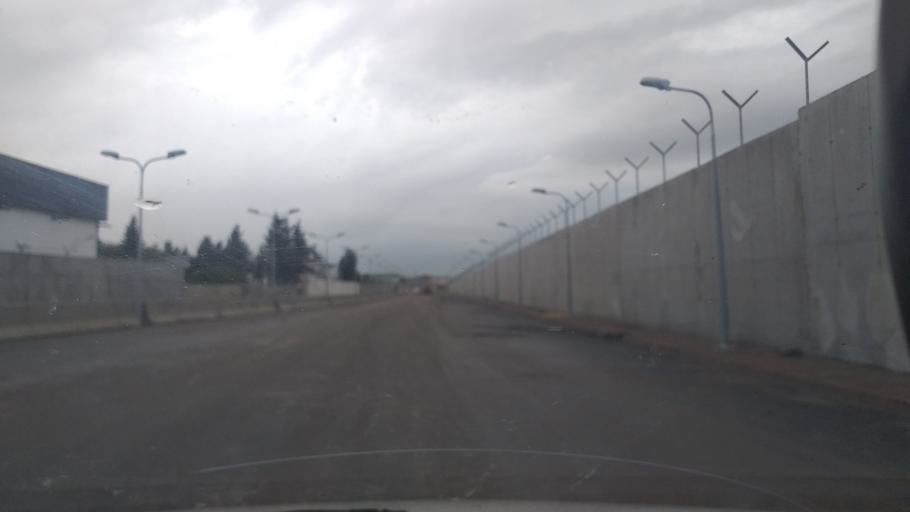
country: TN
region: Ariana
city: Ariana
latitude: 36.8537
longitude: 10.2126
